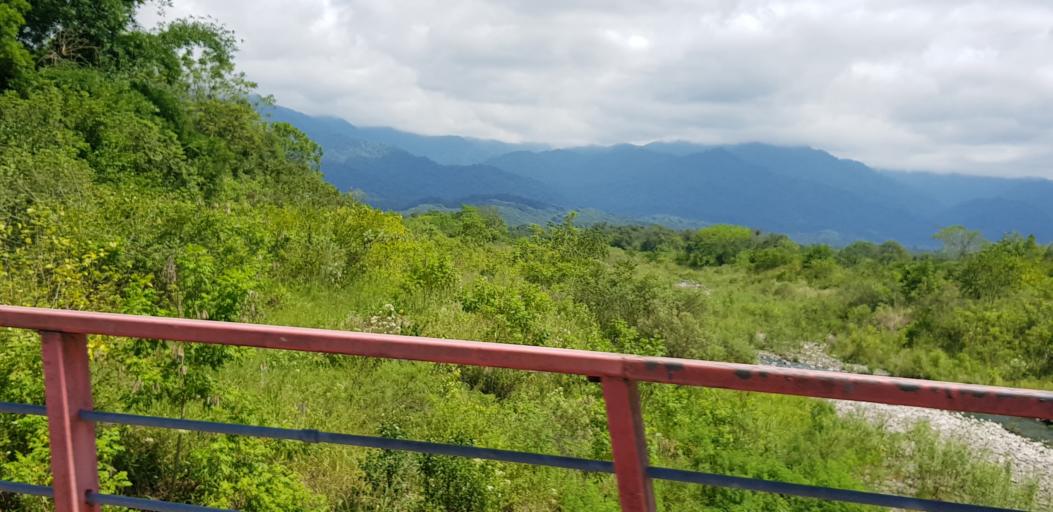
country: AR
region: Tucuman
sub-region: Departamento de Monteros
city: Monteros
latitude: -27.0919
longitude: -65.5539
